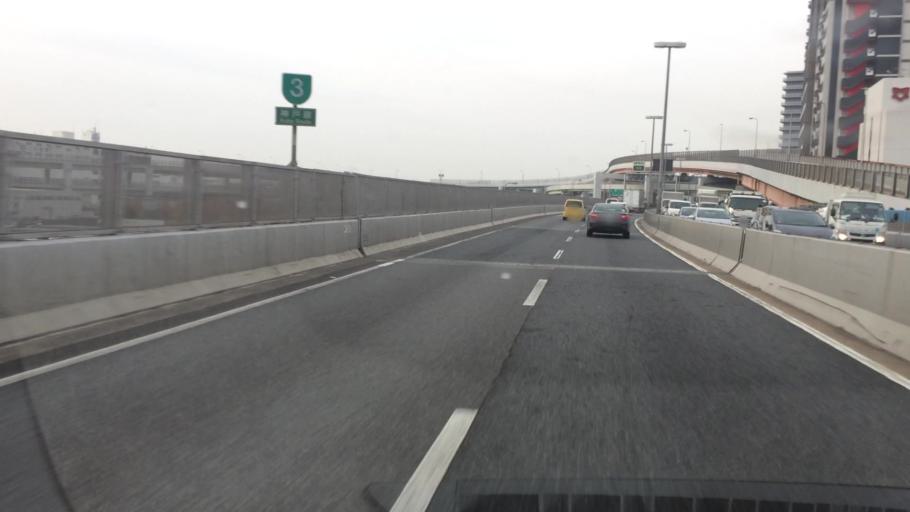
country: JP
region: Hyogo
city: Kobe
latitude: 34.6900
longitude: 135.2017
